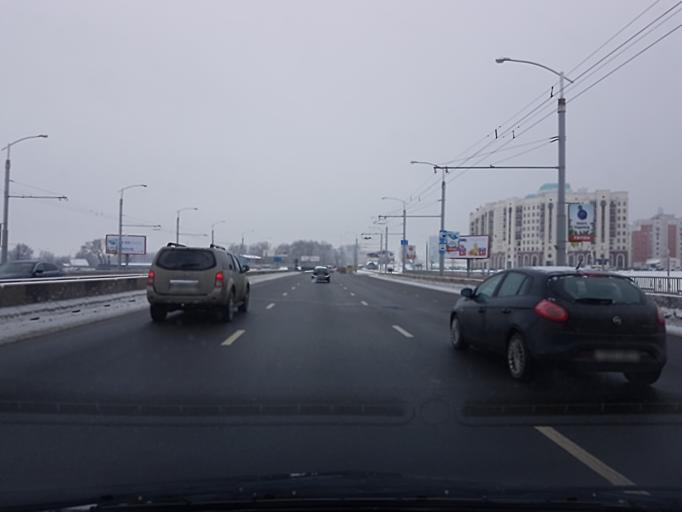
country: BY
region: Minsk
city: Novoye Medvezhino
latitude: 53.8714
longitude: 27.4932
